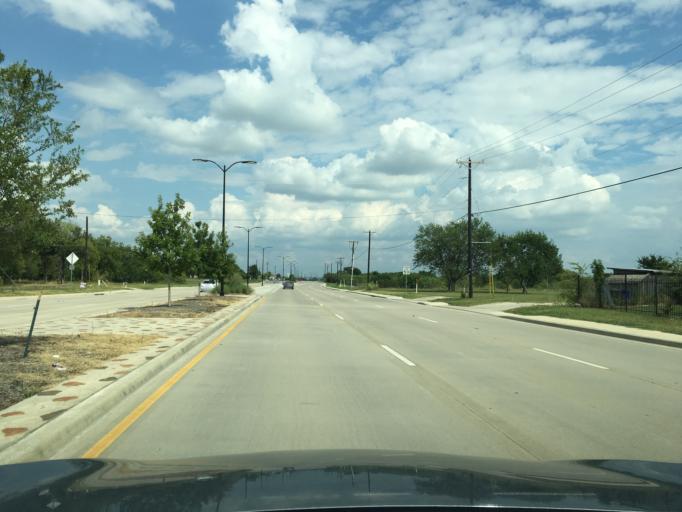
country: US
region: Texas
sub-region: Denton County
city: Oak Point
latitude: 33.1667
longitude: -96.9741
